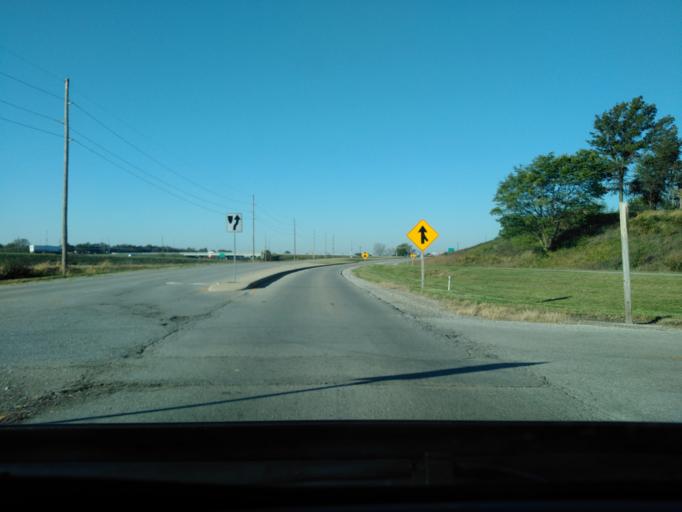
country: US
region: Illinois
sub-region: Bond County
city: Greenville
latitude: 38.8562
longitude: -89.4466
